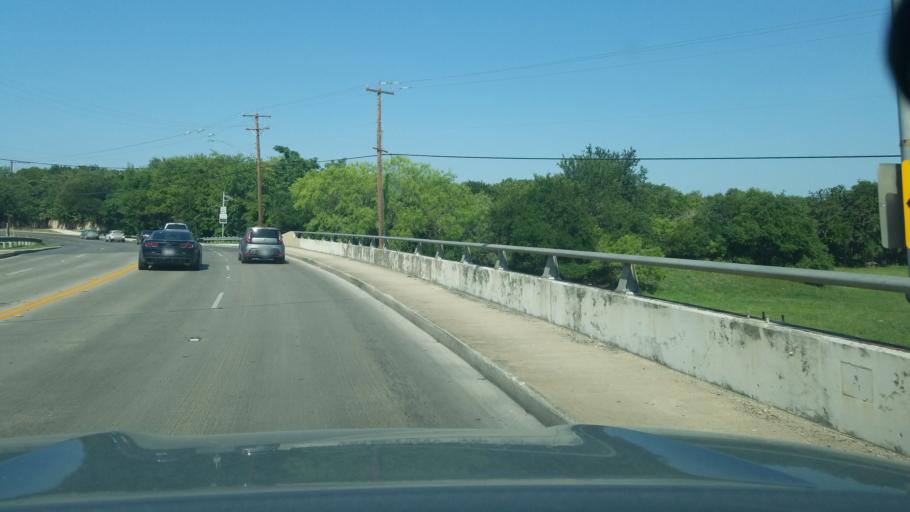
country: US
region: Texas
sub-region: Bexar County
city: Hollywood Park
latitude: 29.5785
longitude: -98.5105
